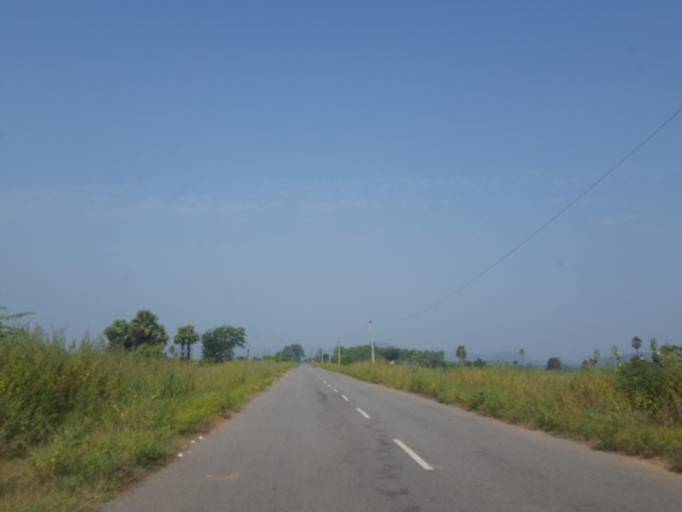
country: IN
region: Telangana
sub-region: Khammam
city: Yellandu
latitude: 17.6444
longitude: 80.2956
